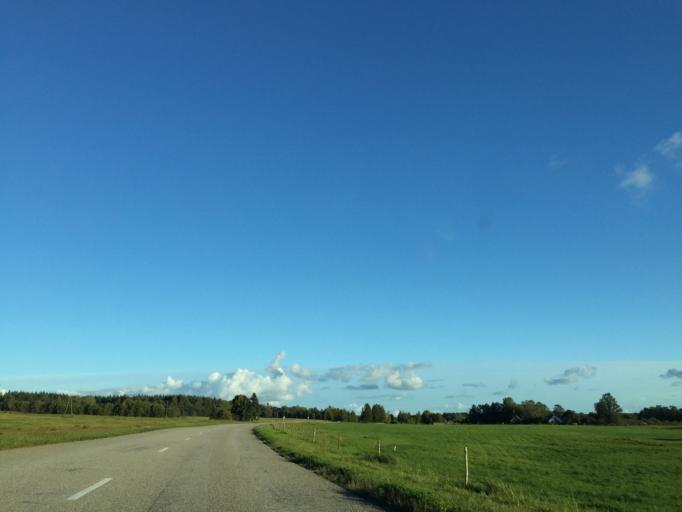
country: LV
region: Kuldigas Rajons
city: Kuldiga
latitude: 56.9276
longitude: 22.0482
